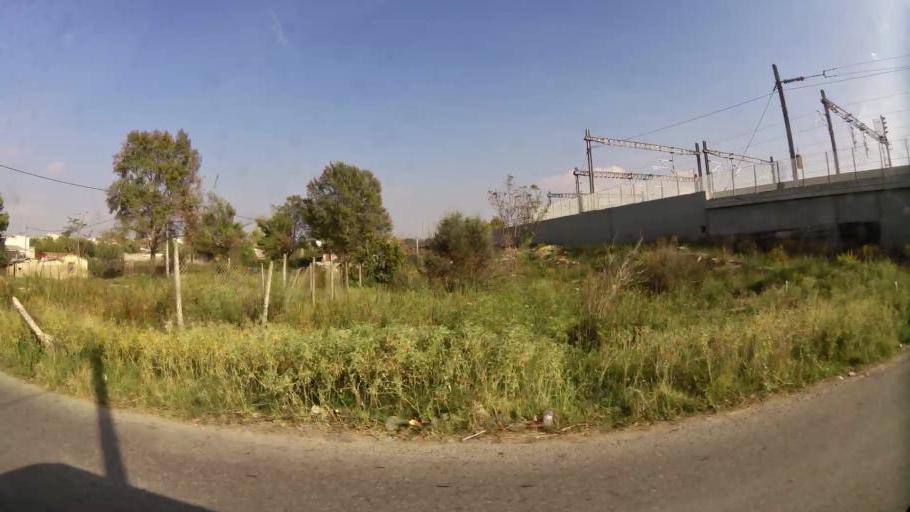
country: GR
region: Attica
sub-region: Nomarchia Anatolikis Attikis
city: Acharnes
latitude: 38.0705
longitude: 23.7323
